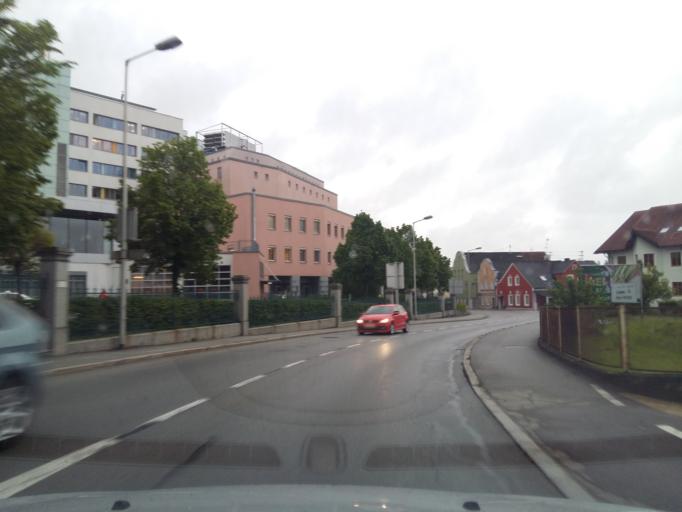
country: AT
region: Upper Austria
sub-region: Politischer Bezirk Scharding
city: Scharding
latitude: 48.4557
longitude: 13.4346
